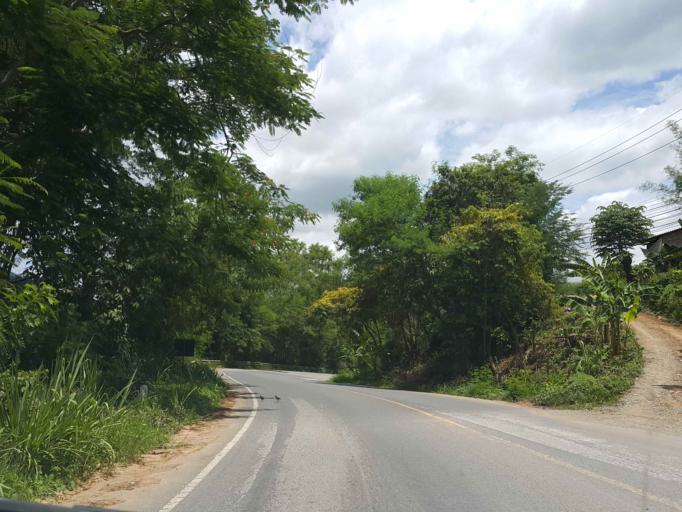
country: TH
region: Chiang Mai
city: Hang Dong
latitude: 18.7656
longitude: 98.8713
